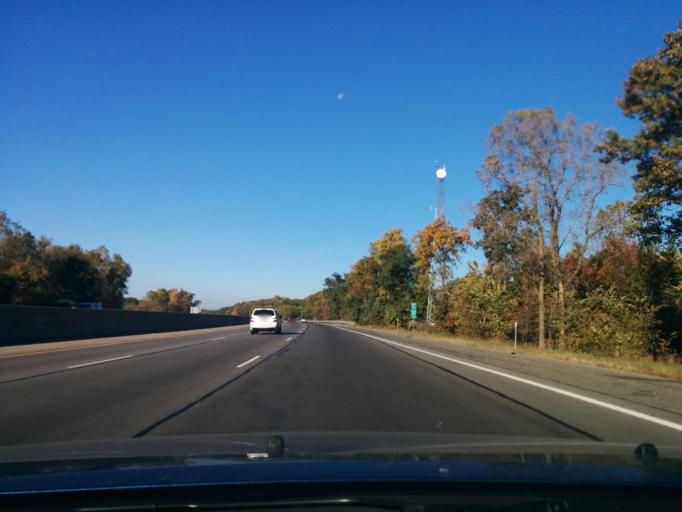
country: US
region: Michigan
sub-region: Oakland County
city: South Lyon
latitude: 42.5214
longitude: -83.6267
